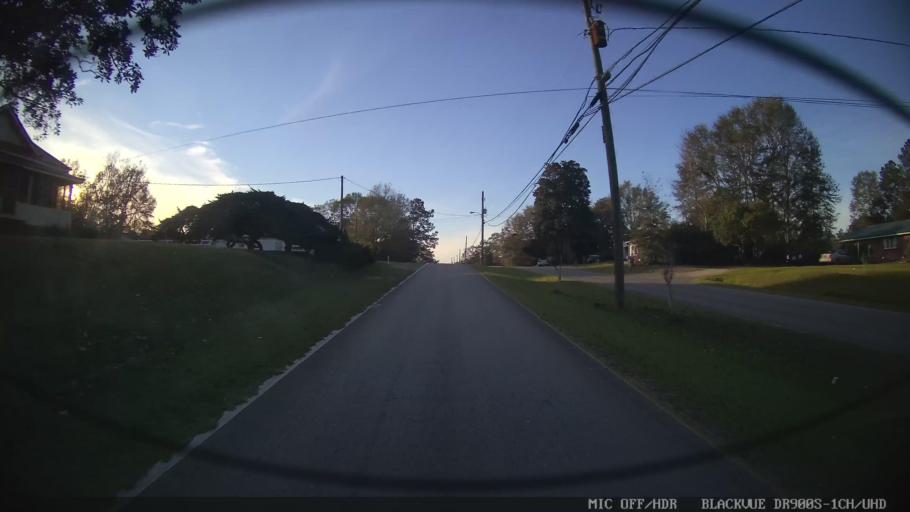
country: US
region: Mississippi
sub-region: Lamar County
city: Lumberton
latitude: 31.0033
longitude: -89.4573
